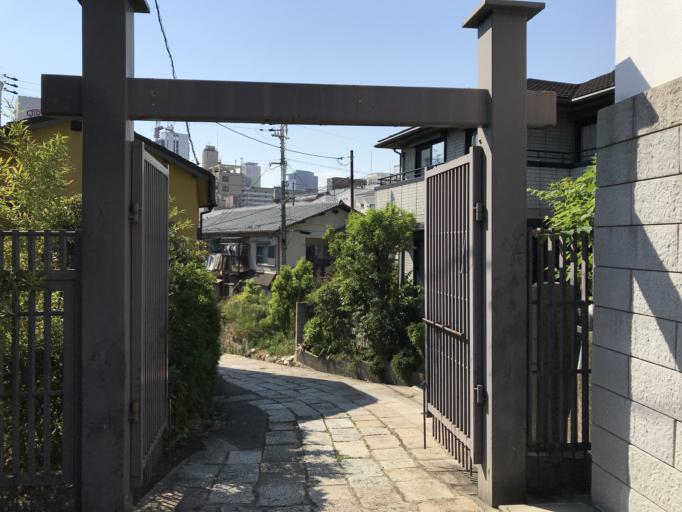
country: JP
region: Osaka
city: Osaka-shi
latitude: 34.6554
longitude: 135.5112
